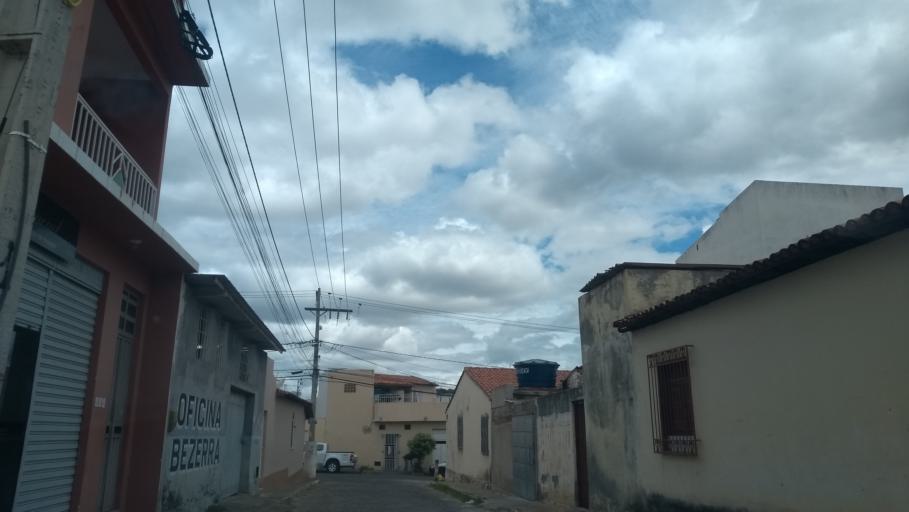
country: BR
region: Bahia
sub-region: Brumado
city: Brumado
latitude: -14.2078
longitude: -41.6700
